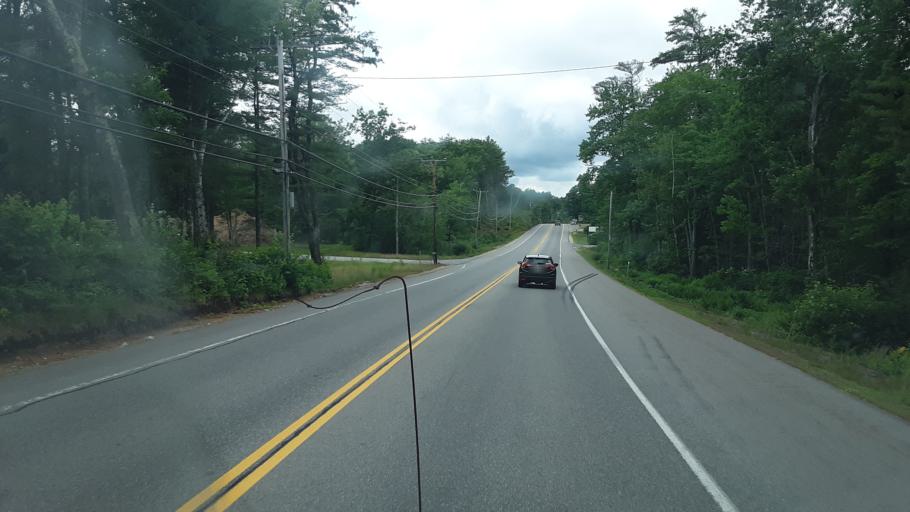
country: US
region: New Hampshire
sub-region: Rockingham County
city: Northwood
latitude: 43.2206
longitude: -71.2335
